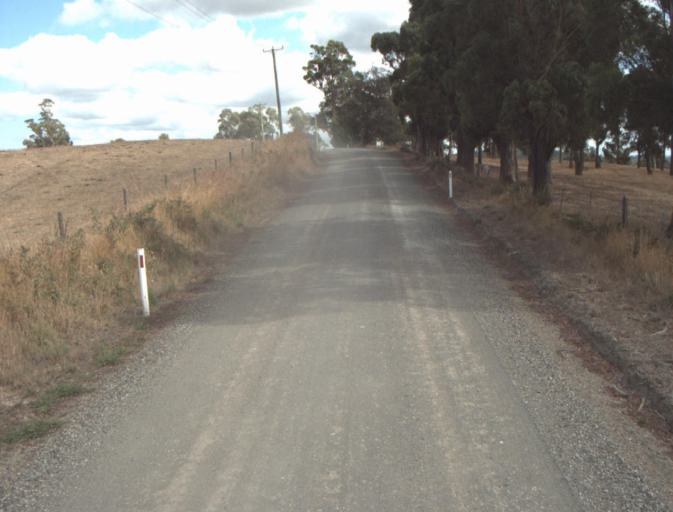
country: AU
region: Tasmania
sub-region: Launceston
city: Mayfield
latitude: -41.2193
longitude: 147.1425
